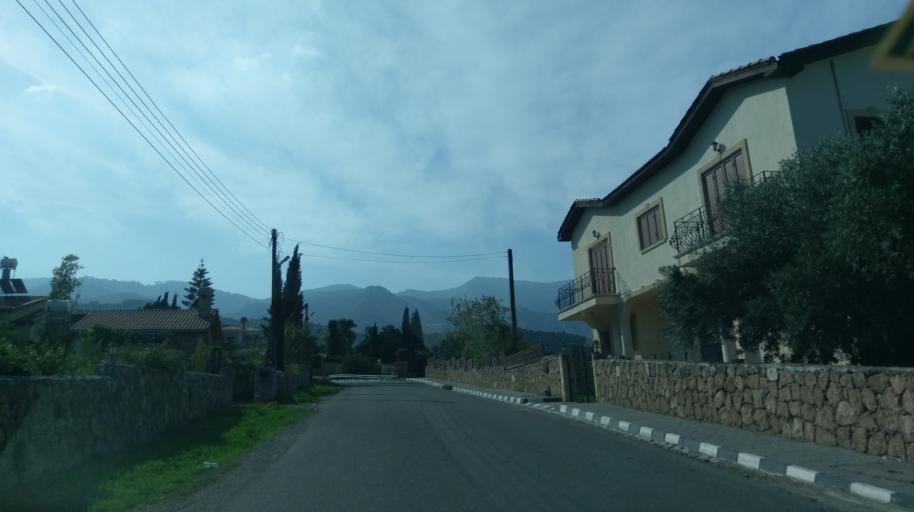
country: CY
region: Keryneia
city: Lapithos
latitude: 35.3392
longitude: 33.2175
